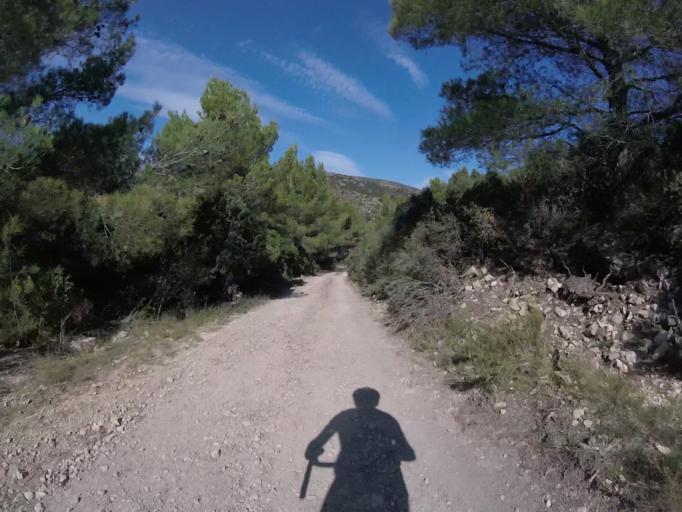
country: ES
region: Valencia
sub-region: Provincia de Castello
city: Sarratella
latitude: 40.2735
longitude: 0.0319
